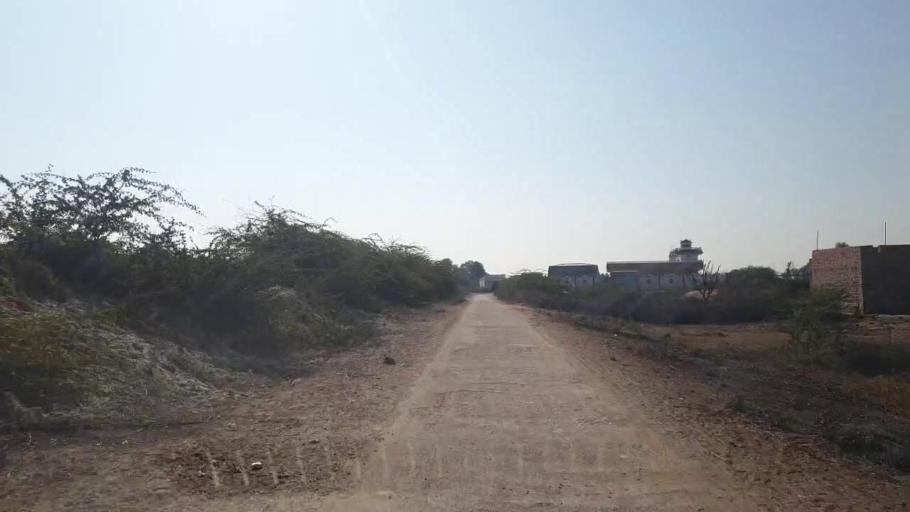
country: PK
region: Sindh
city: Shahpur Chakar
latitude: 26.0792
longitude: 68.6481
